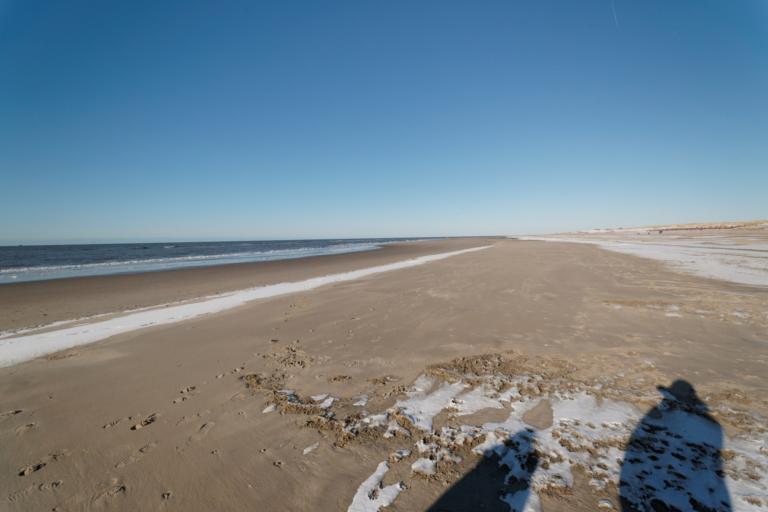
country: NL
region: North Holland
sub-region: Gemeente Texel
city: Den Burg
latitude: 53.1572
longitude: 4.8140
